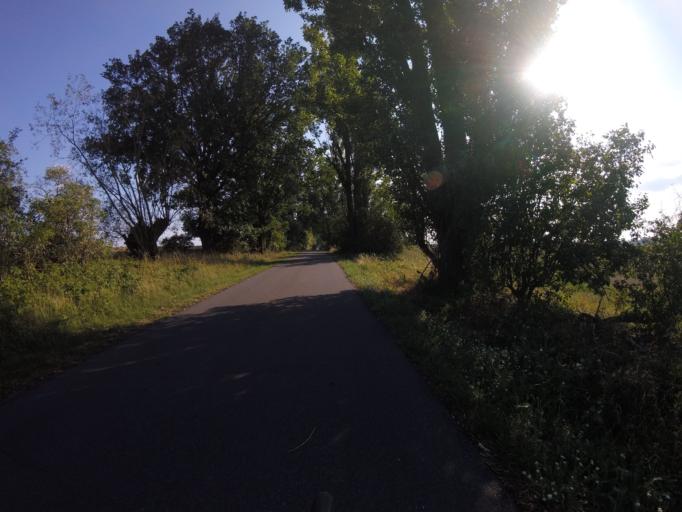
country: DE
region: Brandenburg
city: Bliesdorf
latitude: 52.6715
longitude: 14.1325
